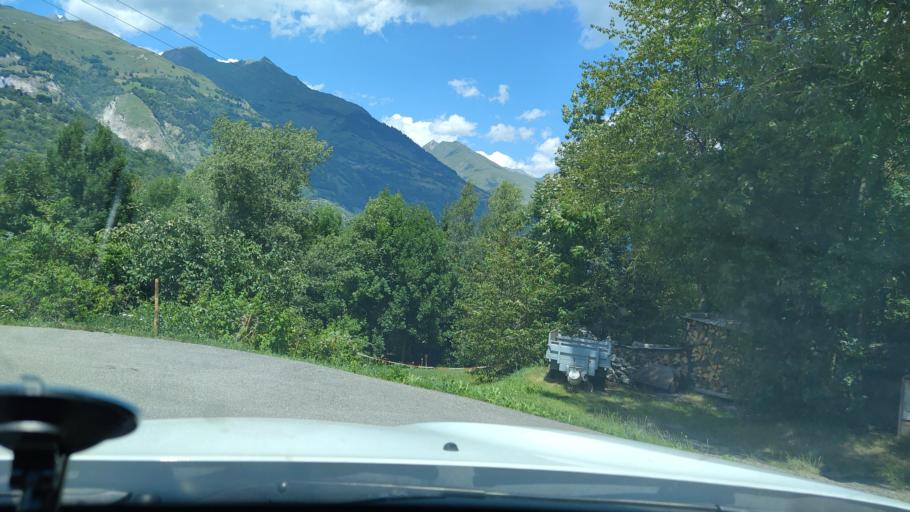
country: FR
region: Rhone-Alpes
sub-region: Departement de la Savoie
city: Bourg-Saint-Maurice
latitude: 45.5973
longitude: 6.7628
